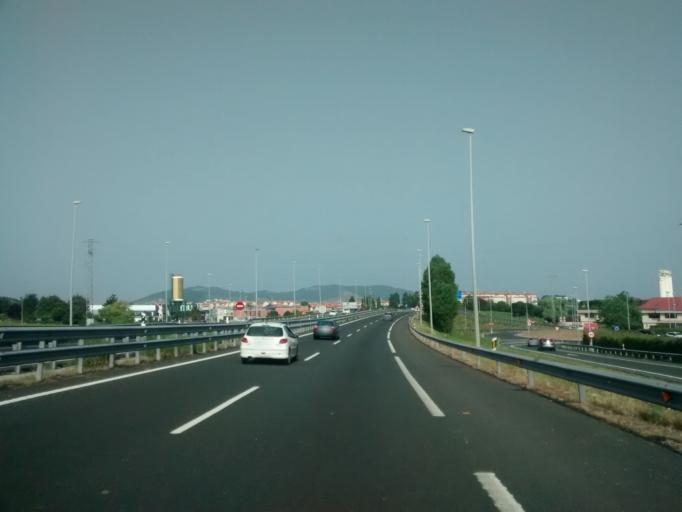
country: ES
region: Cantabria
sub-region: Provincia de Cantabria
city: Santa Cruz de Bezana
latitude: 43.4389
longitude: -3.8865
